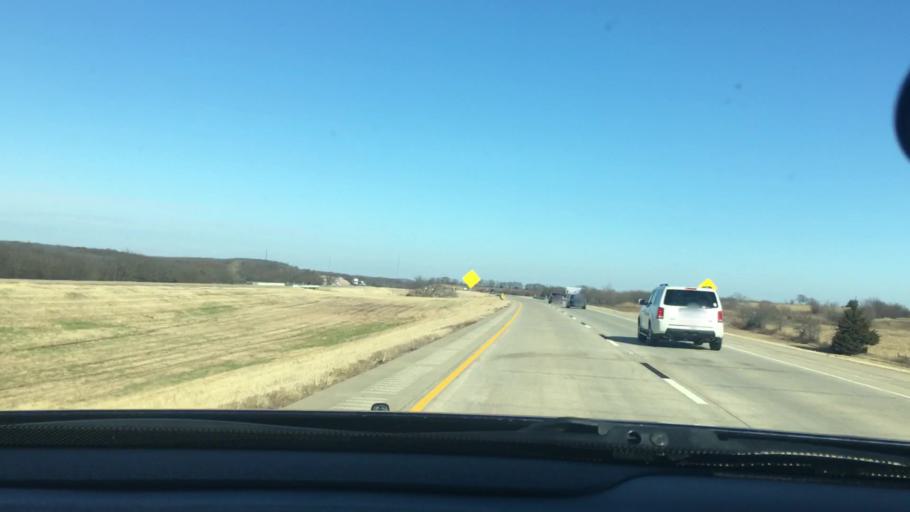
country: US
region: Oklahoma
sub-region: Love County
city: Marietta
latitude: 33.9744
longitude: -97.1340
